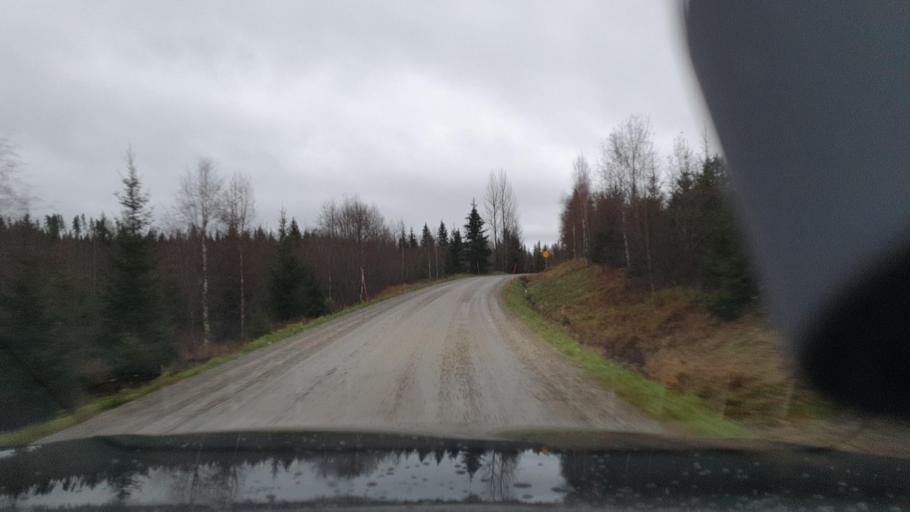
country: SE
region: Vaermland
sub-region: Arvika Kommun
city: Arvika
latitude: 59.8374
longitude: 12.7456
